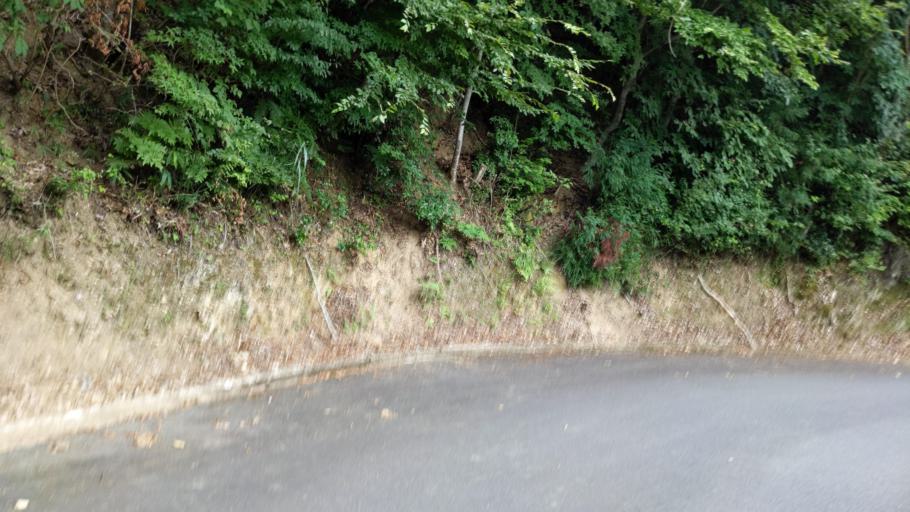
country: JP
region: Kyoto
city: Maizuru
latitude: 35.3894
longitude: 135.4390
